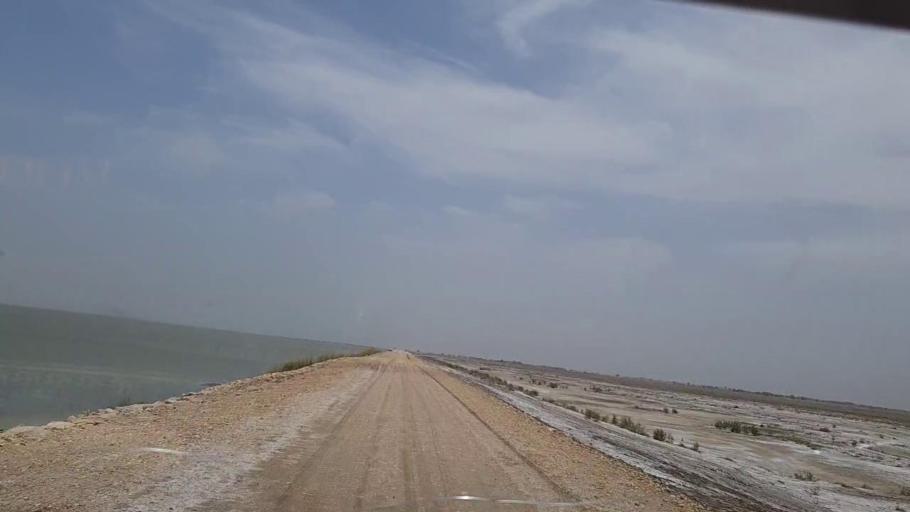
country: PK
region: Sindh
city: Sehwan
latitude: 26.4131
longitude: 67.7775
